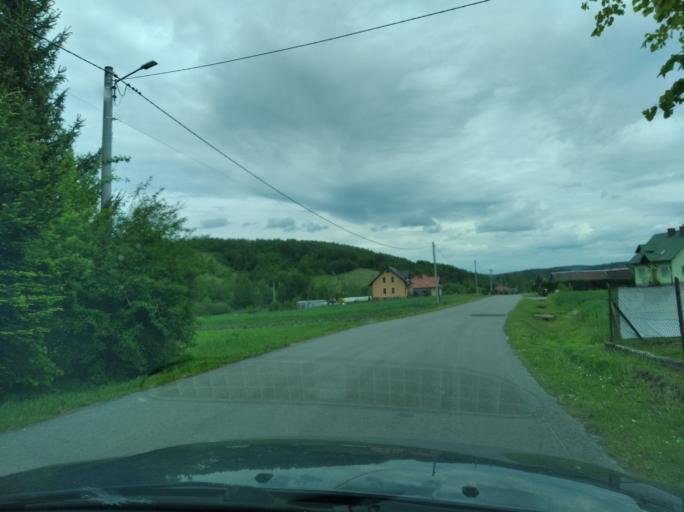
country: PL
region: Subcarpathian Voivodeship
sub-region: Powiat przemyski
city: Przedmiescie Dubieckie
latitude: 49.8340
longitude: 22.3210
